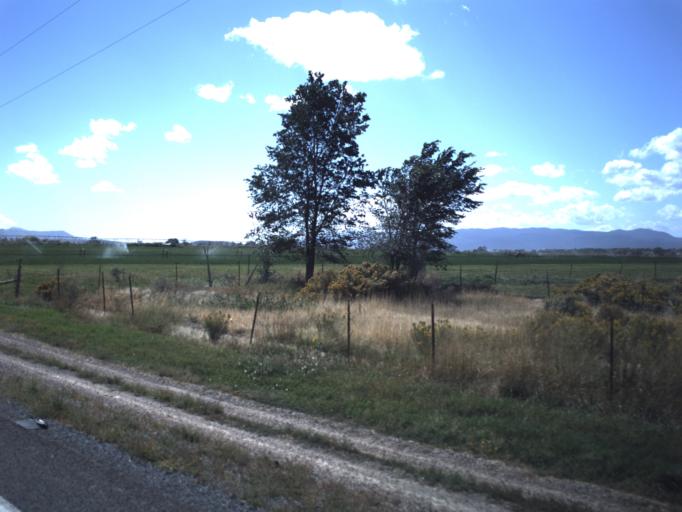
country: US
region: Utah
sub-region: Iron County
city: Enoch
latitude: 37.7415
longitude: -113.0553
